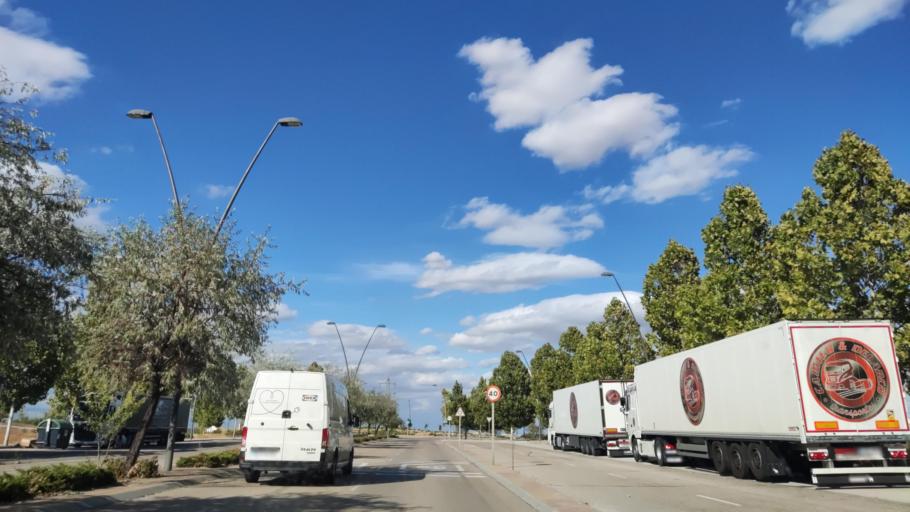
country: ES
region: Madrid
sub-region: Provincia de Madrid
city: Pinto
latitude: 40.2852
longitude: -3.6775
